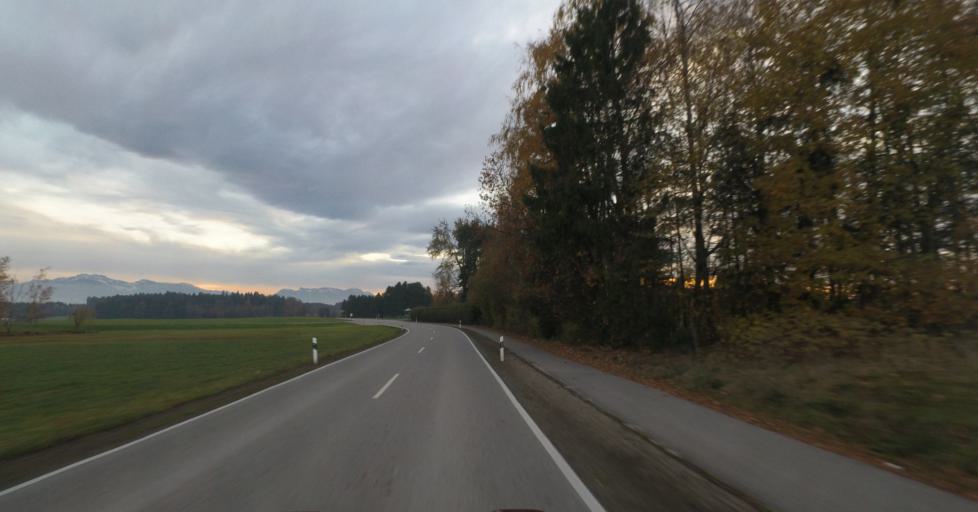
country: DE
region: Bavaria
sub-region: Upper Bavaria
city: Eggstatt
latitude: 47.9046
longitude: 12.3691
